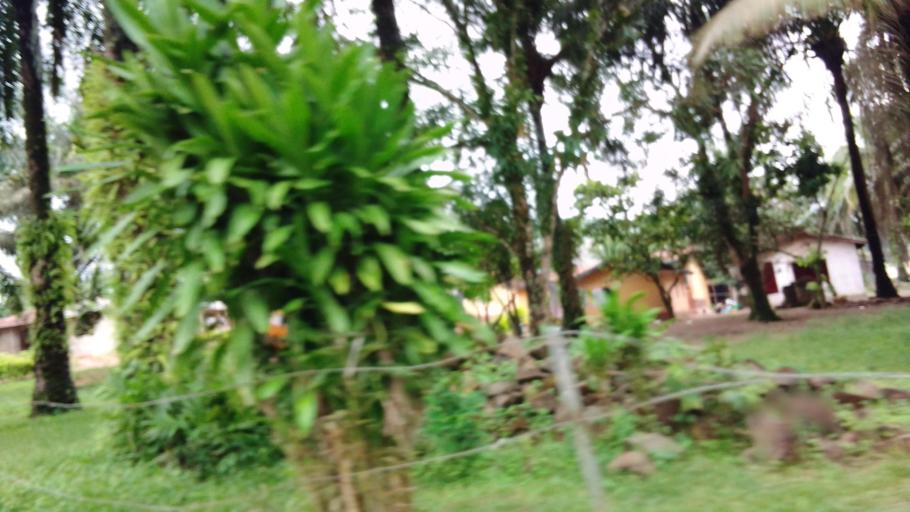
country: SL
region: Eastern Province
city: Kenema
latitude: 7.8553
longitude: -11.1873
